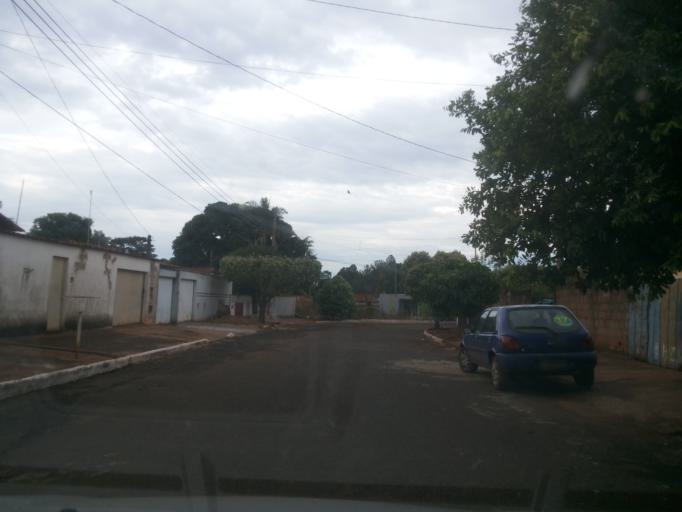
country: BR
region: Minas Gerais
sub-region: Ituiutaba
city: Ituiutaba
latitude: -18.9763
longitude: -49.4805
